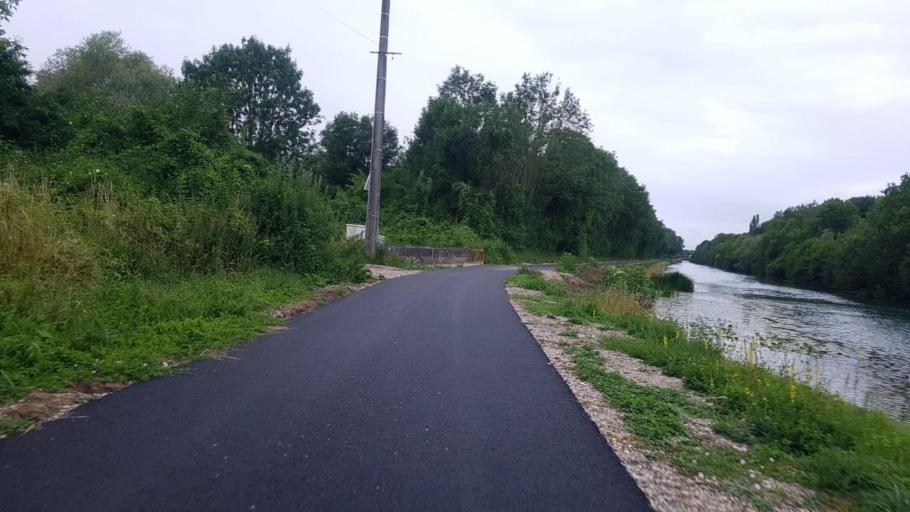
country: FR
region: Champagne-Ardenne
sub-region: Departement de la Marne
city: Sarry
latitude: 48.8389
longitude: 4.5056
